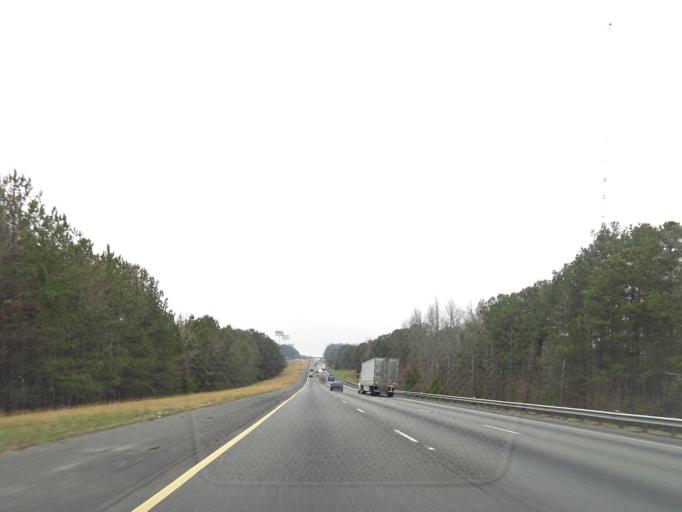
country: US
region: Georgia
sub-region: Henry County
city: Locust Grove
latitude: 33.3678
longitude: -84.1324
